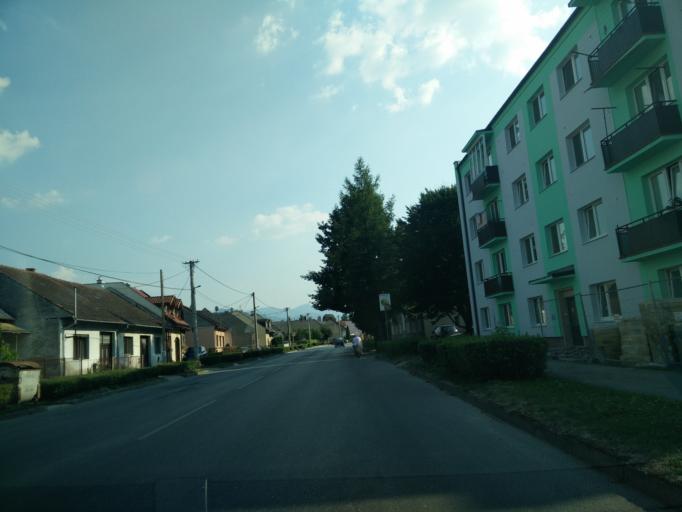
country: SK
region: Zilinsky
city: Rajec
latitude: 49.0916
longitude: 18.6392
